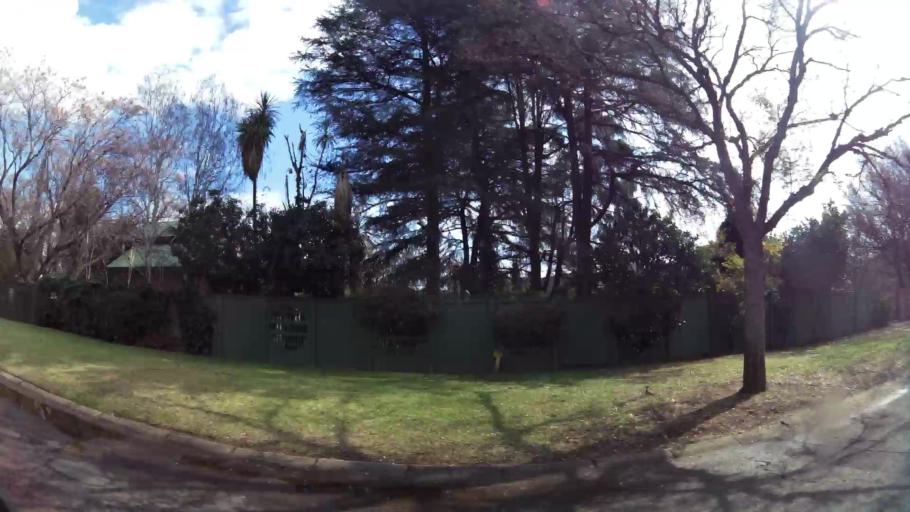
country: ZA
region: Gauteng
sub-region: Sedibeng District Municipality
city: Vanderbijlpark
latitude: -26.7393
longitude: 27.8365
